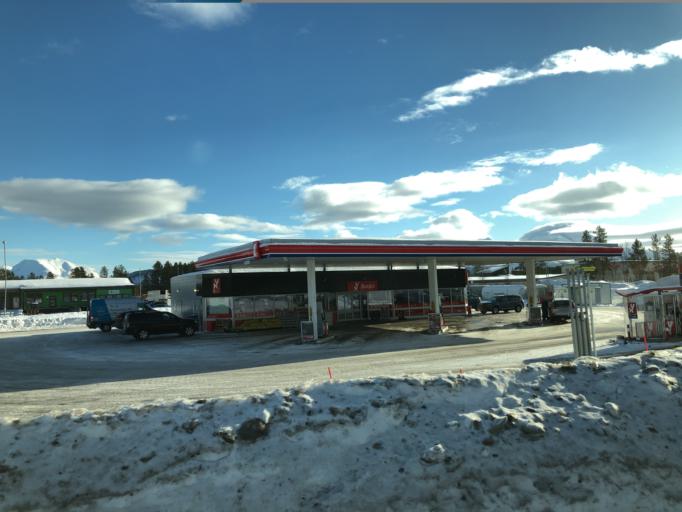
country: NO
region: Troms
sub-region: Malselv
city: Moen
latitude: 69.0940
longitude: 18.5929
